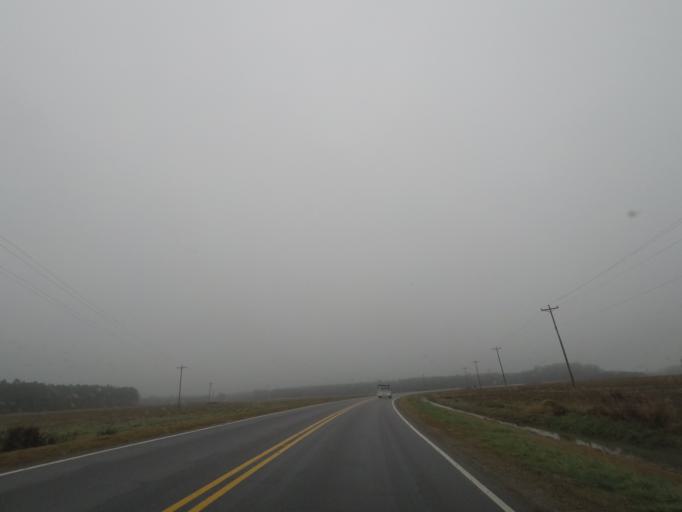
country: US
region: North Carolina
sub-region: Scotland County
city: Laurinburg
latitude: 34.7961
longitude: -79.4283
